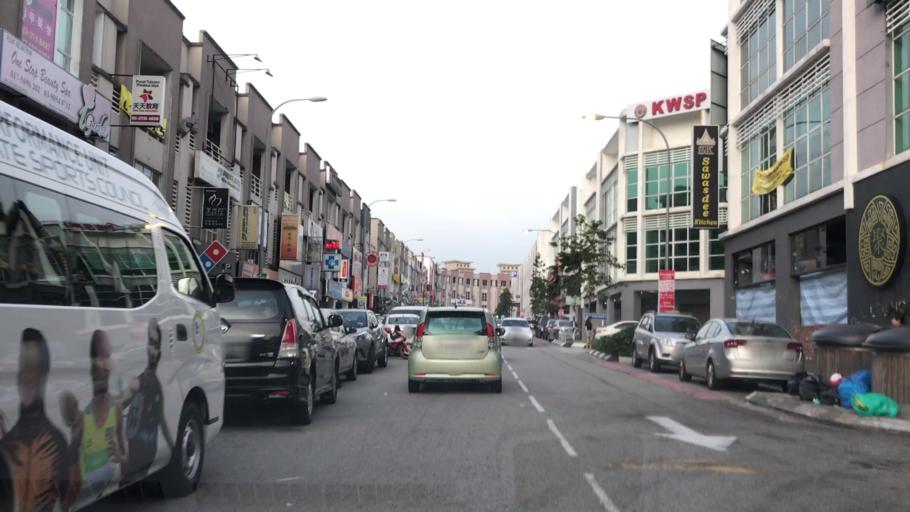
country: MY
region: Selangor
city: Kampong Baharu Balakong
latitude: 3.0710
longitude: 101.6923
